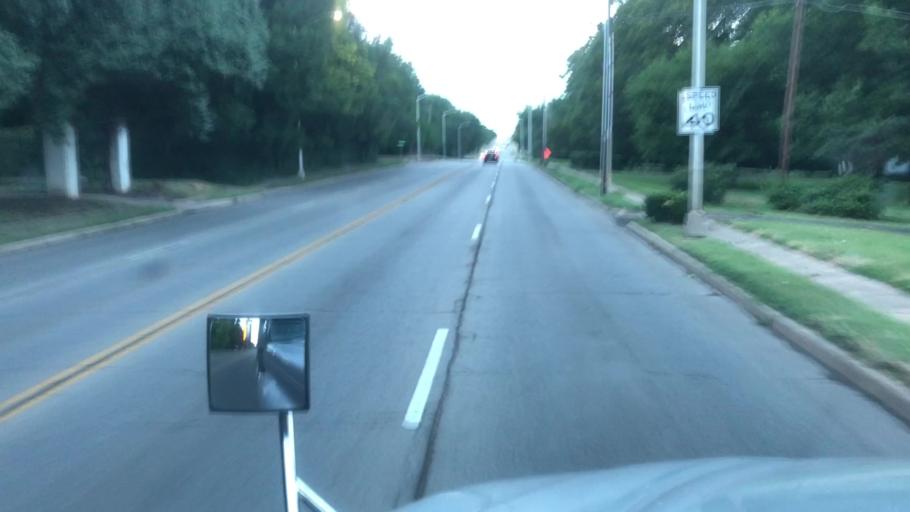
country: US
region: Oklahoma
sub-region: Kay County
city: Ponca City
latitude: 36.7159
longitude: -97.0672
